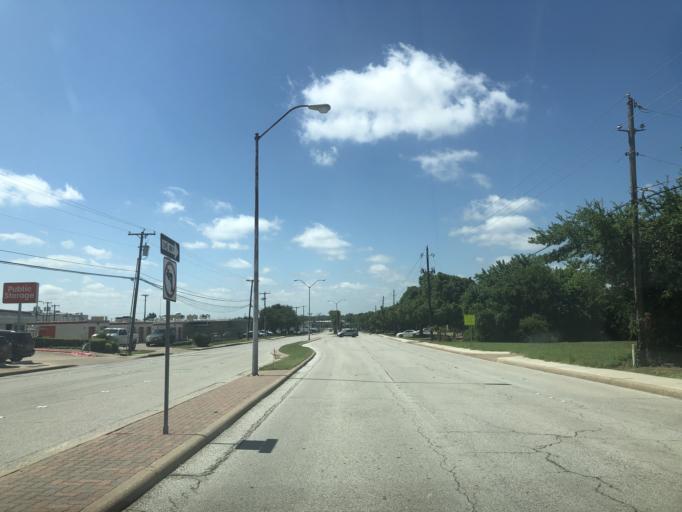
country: US
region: Texas
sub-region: Dallas County
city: Duncanville
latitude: 32.6462
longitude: -96.9255
